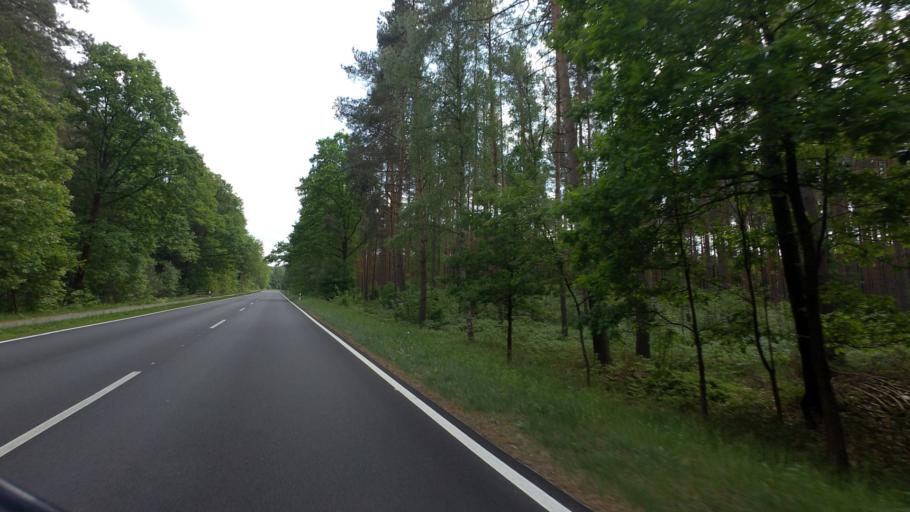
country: DE
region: Saxony
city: Niesky
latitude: 51.3314
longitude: 14.8147
